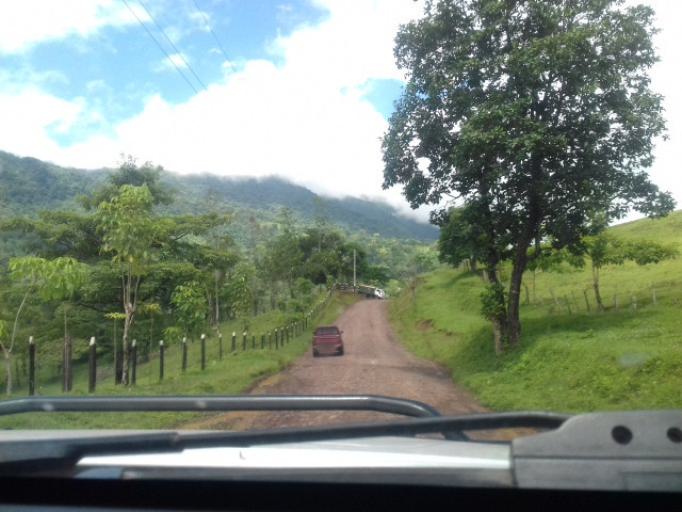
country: NI
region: Matagalpa
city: Rio Blanco
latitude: 12.9819
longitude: -85.1877
